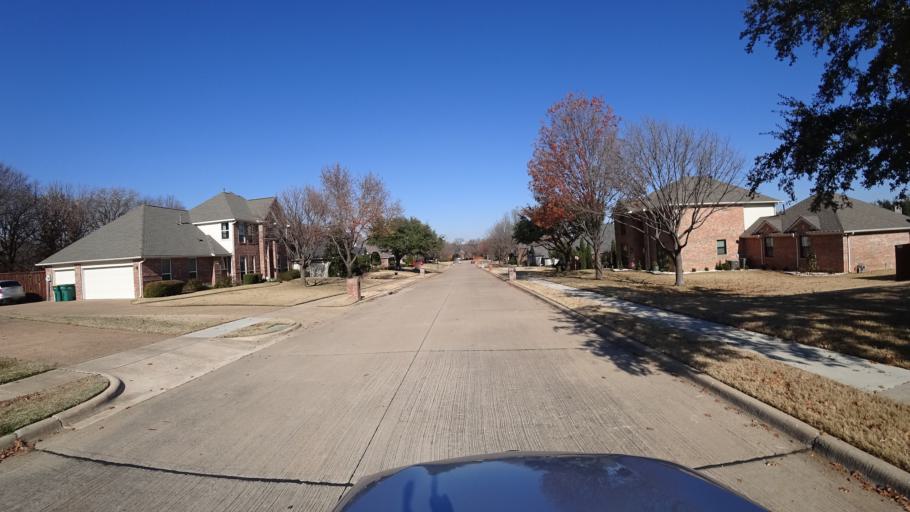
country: US
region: Texas
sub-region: Denton County
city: Lewisville
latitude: 33.0161
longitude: -97.0158
